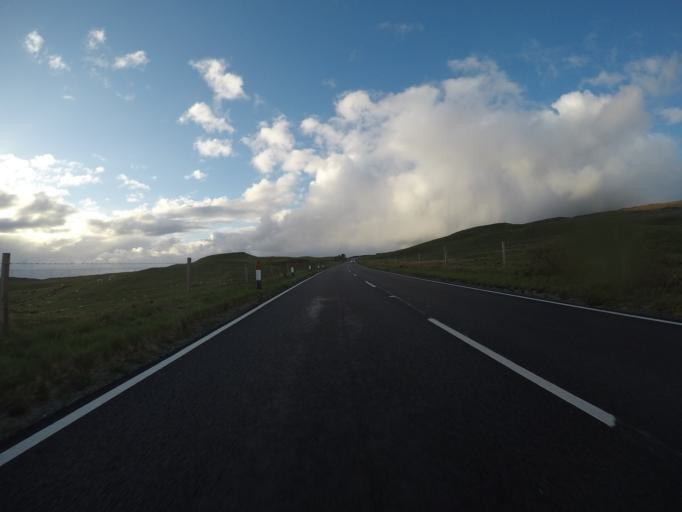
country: GB
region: Scotland
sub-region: Highland
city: Portree
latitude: 57.5426
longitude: -6.3649
